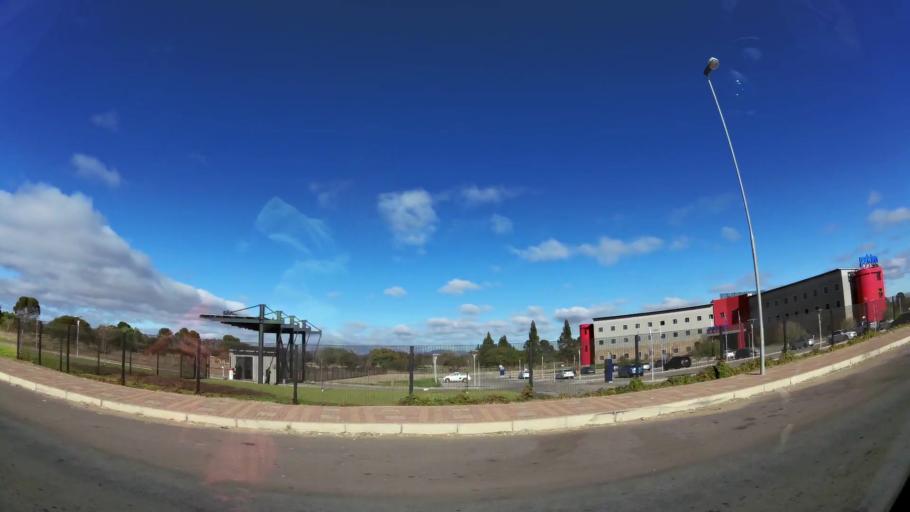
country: ZA
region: Limpopo
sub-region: Capricorn District Municipality
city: Polokwane
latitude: -23.9263
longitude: 29.4646
